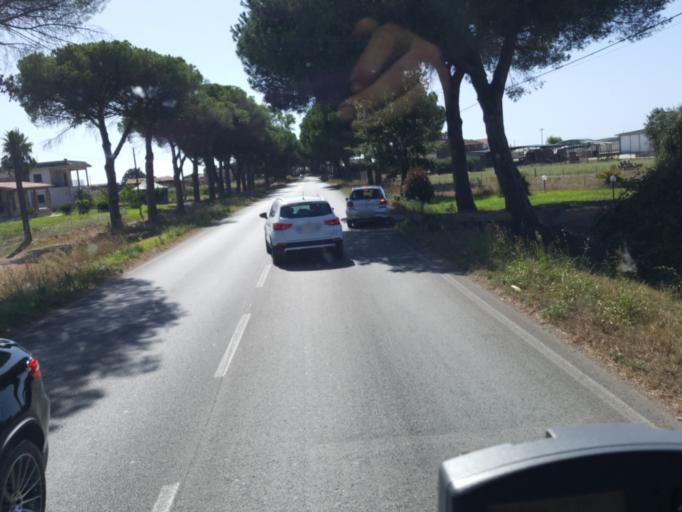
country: IT
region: Latium
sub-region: Citta metropolitana di Roma Capitale
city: Nettuno
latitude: 41.5117
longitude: 12.6967
